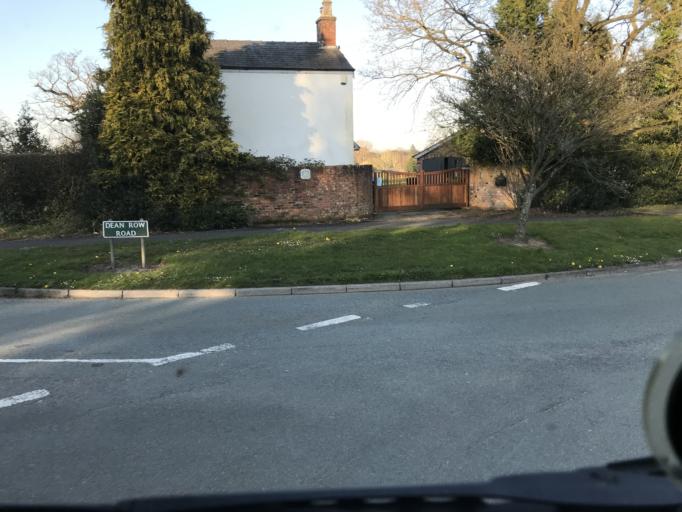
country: GB
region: England
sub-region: Cheshire East
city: Mottram St. Andrew
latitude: 53.3309
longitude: -2.1933
